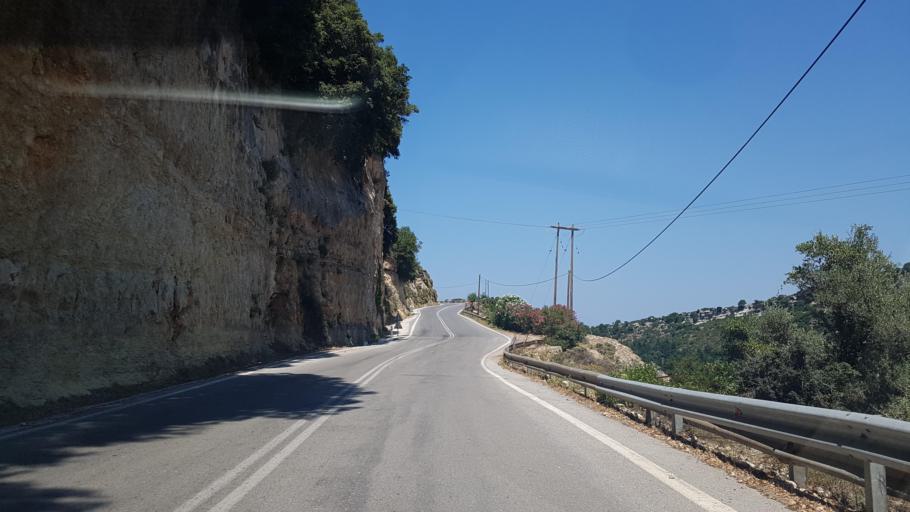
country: GR
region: Crete
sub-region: Nomos Rethymnis
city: Agia Foteini
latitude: 35.3156
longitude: 24.6251
